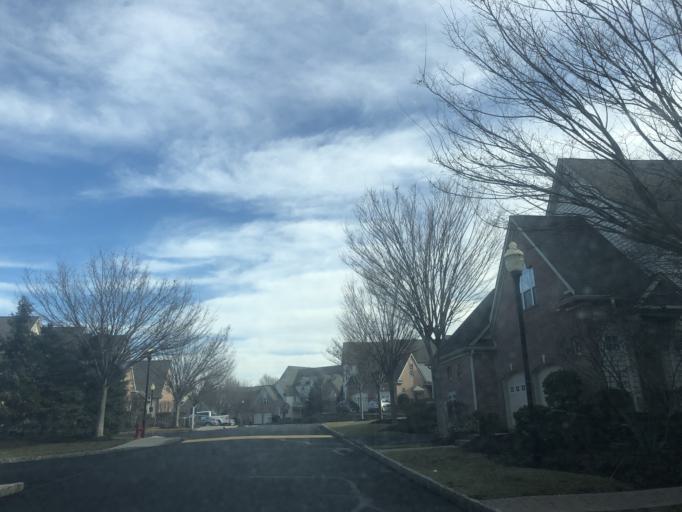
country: US
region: New Jersey
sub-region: Somerset County
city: Kingston
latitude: 40.3618
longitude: -74.6193
